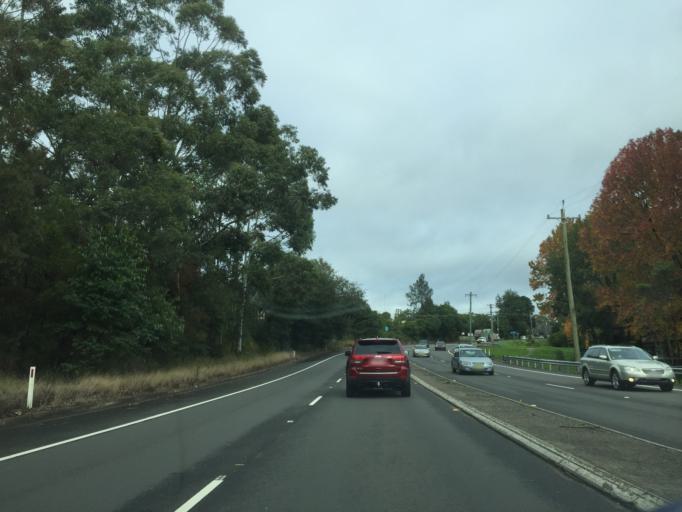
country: AU
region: New South Wales
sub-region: Blue Mountains Municipality
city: Blaxland
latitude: -33.6995
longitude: 150.5615
